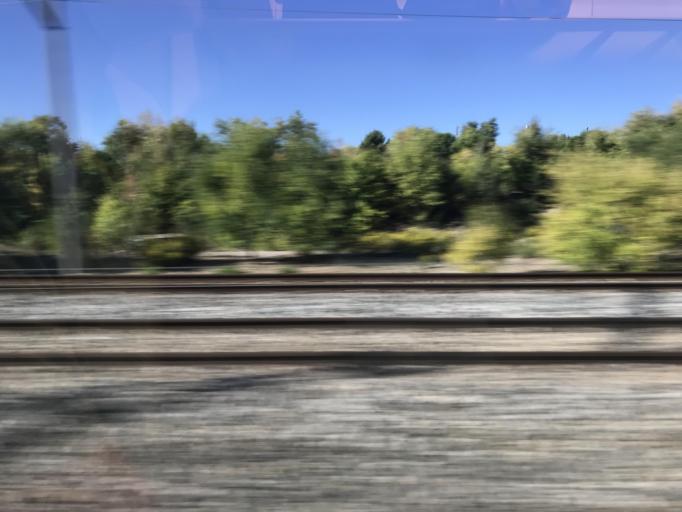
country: ES
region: Madrid
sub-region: Provincia de Madrid
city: Las Tablas
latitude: 40.5217
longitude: -3.6859
